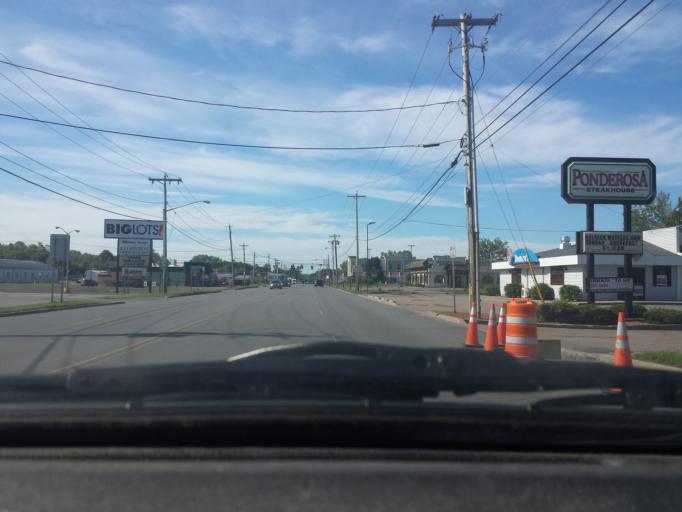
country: US
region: New York
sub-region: St. Lawrence County
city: Potsdam
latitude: 44.6853
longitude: -74.9871
